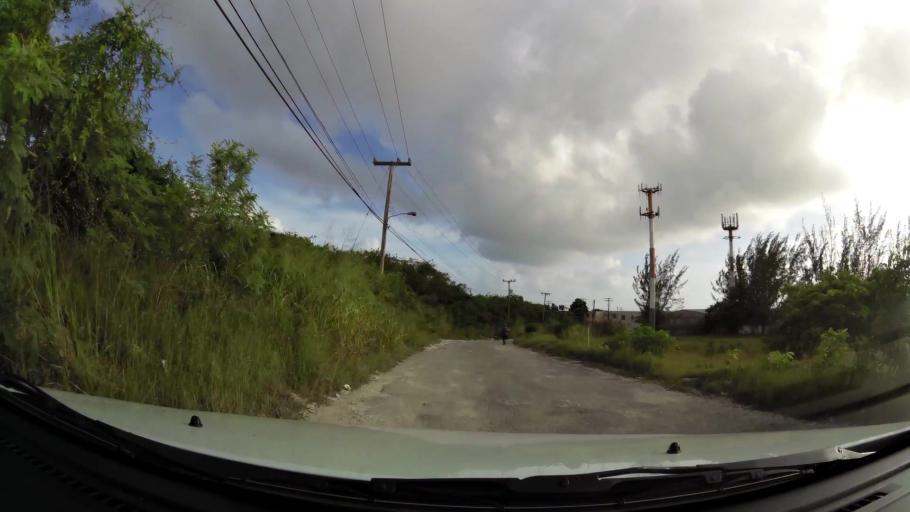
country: BB
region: Christ Church
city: Oistins
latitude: 13.0810
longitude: -59.5346
